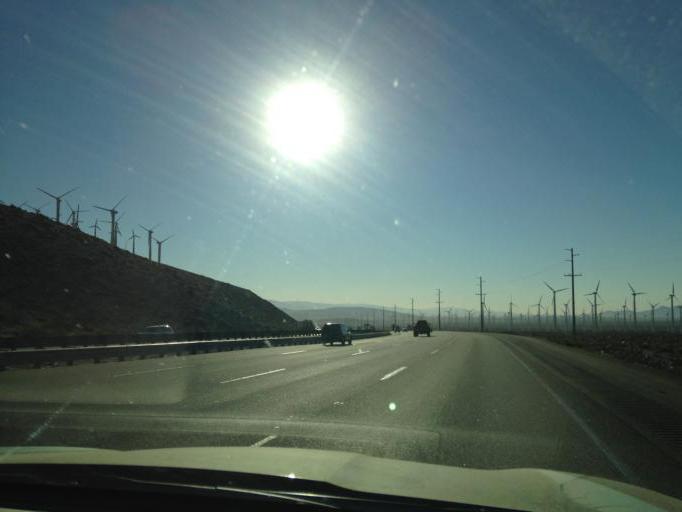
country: US
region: California
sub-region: Riverside County
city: Garnet
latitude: 33.9198
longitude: -116.6287
